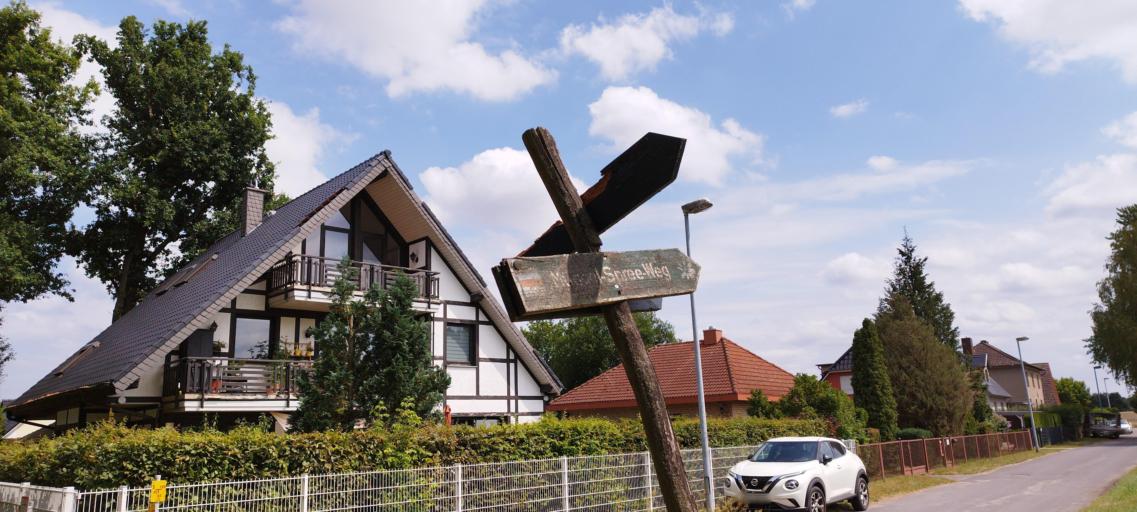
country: DE
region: Brandenburg
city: Schoneiche
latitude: 52.4847
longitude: 13.7082
